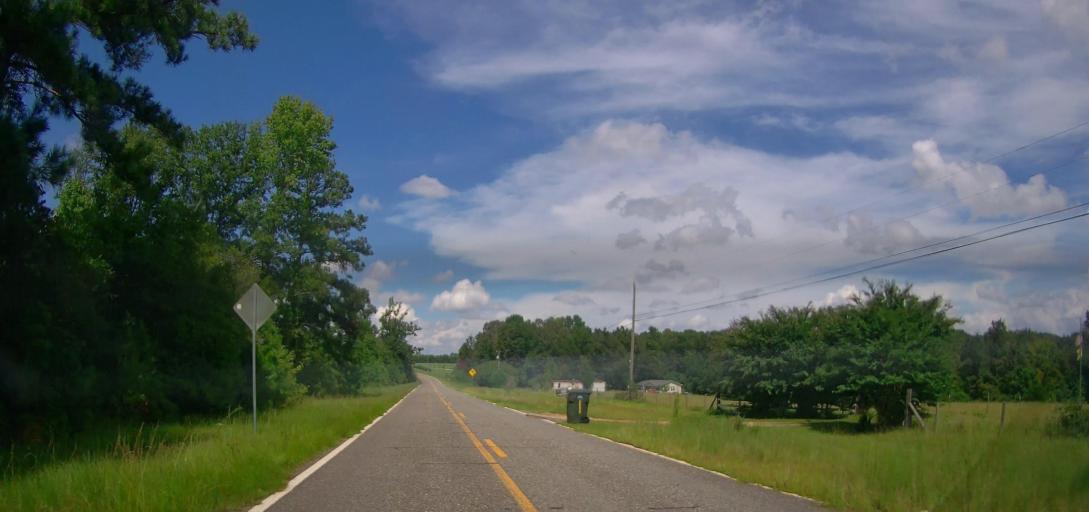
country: US
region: Georgia
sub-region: Peach County
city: Fort Valley
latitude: 32.5228
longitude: -83.8268
